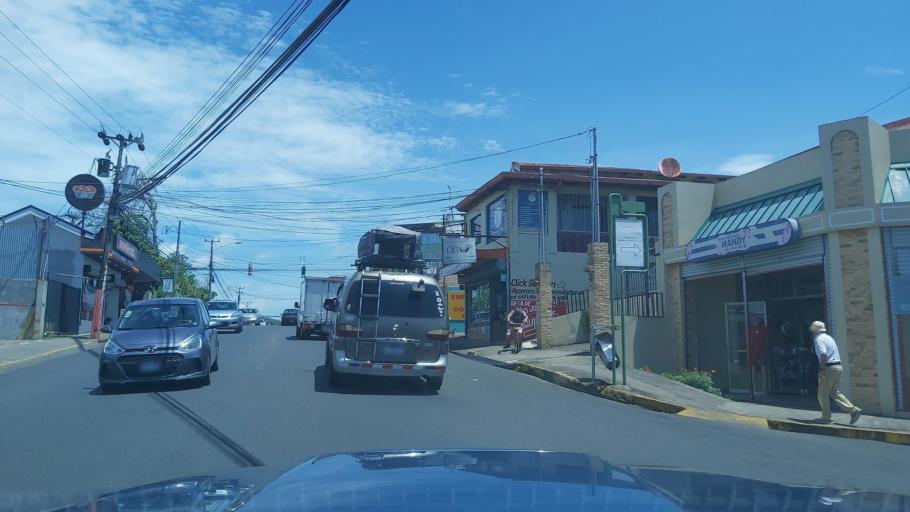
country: CR
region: Alajuela
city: San Juan
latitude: 10.0904
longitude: -84.3467
